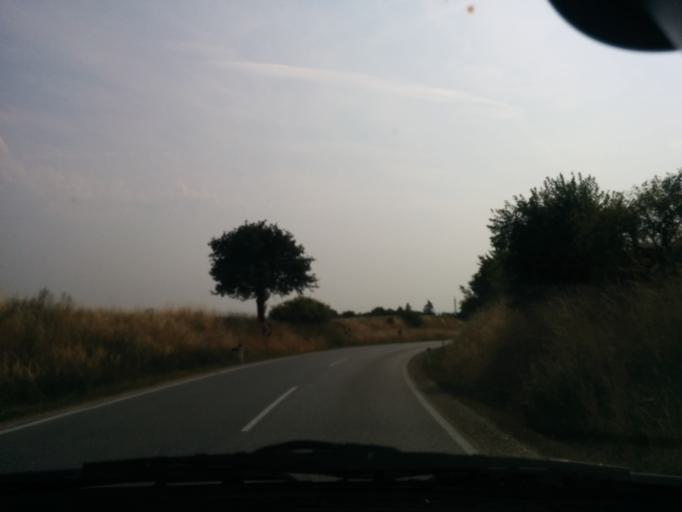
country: AT
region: Lower Austria
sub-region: Politischer Bezirk Horn
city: Rohrenbach
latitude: 48.6474
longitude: 15.5391
